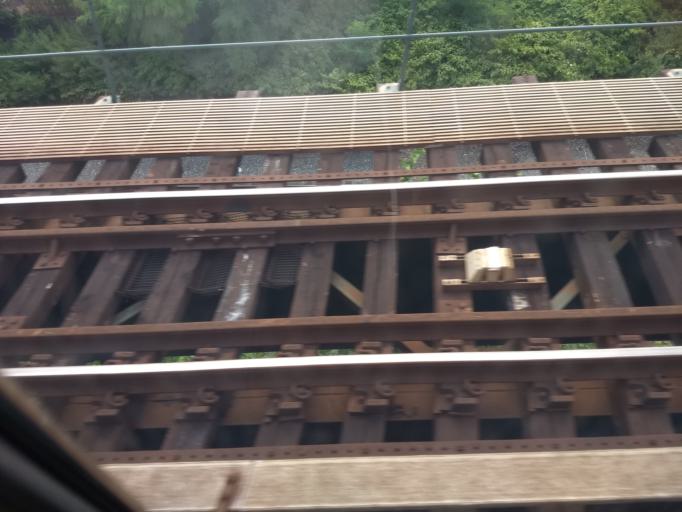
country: US
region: New York
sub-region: Kings County
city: East New York
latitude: 40.6659
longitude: -73.9010
